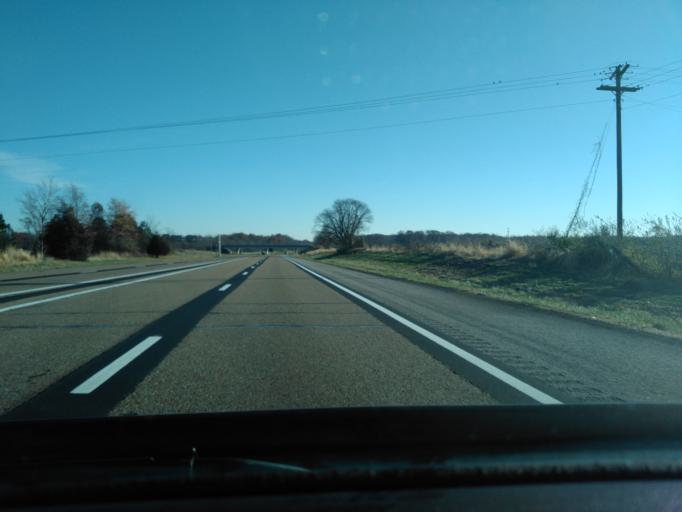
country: US
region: Illinois
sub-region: Madison County
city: Troy
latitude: 38.7520
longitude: -89.8982
